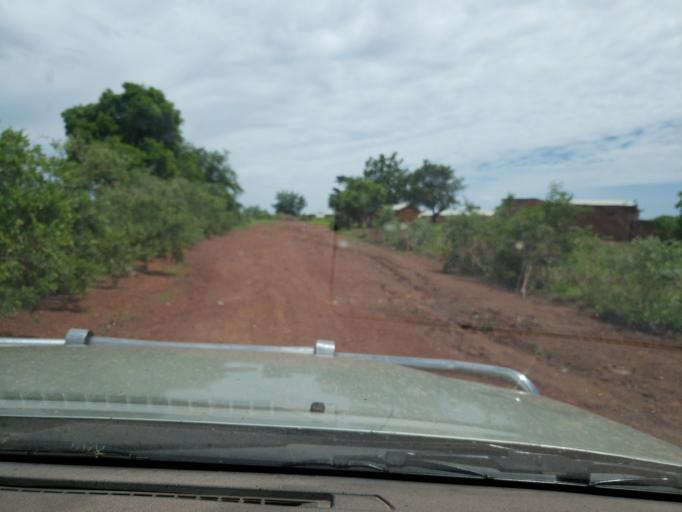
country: ML
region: Sikasso
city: Sikasso
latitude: 11.6756
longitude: -6.1742
